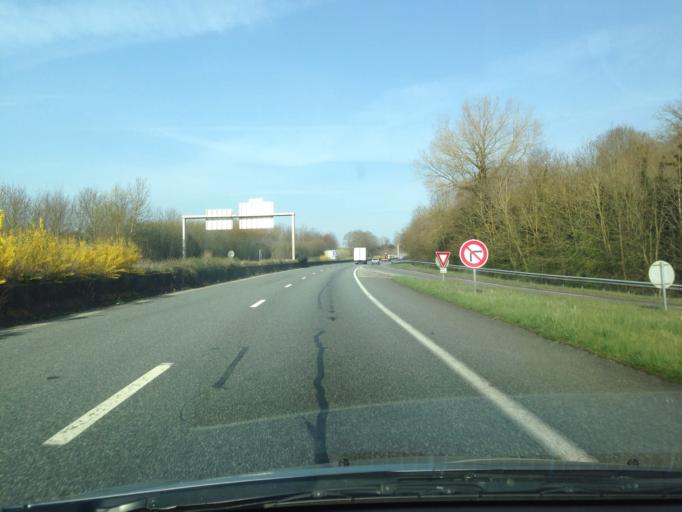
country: FR
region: Picardie
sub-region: Departement de la Somme
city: Abbeville
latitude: 50.1283
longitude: 1.8000
